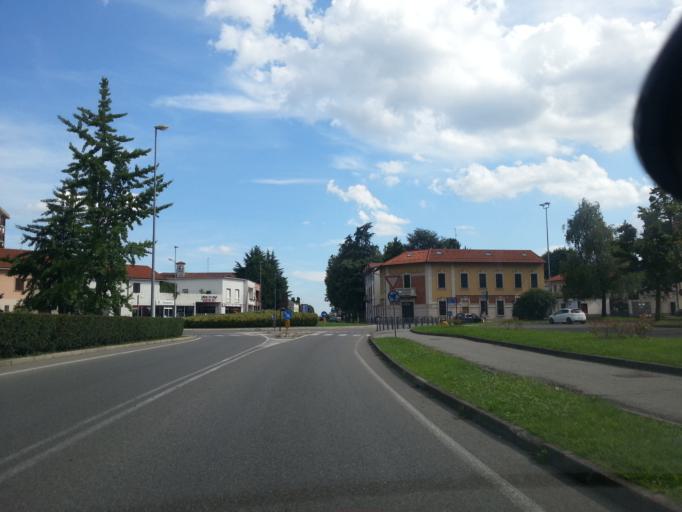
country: IT
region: Lombardy
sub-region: Provincia di Monza e Brianza
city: Albiate
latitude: 45.6582
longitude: 9.2526
